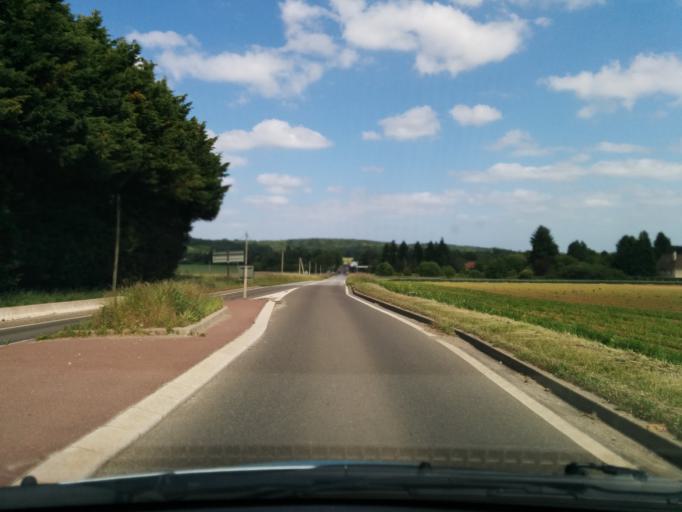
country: FR
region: Ile-de-France
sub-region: Departement des Yvelines
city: Crespieres
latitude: 48.8866
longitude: 1.9149
